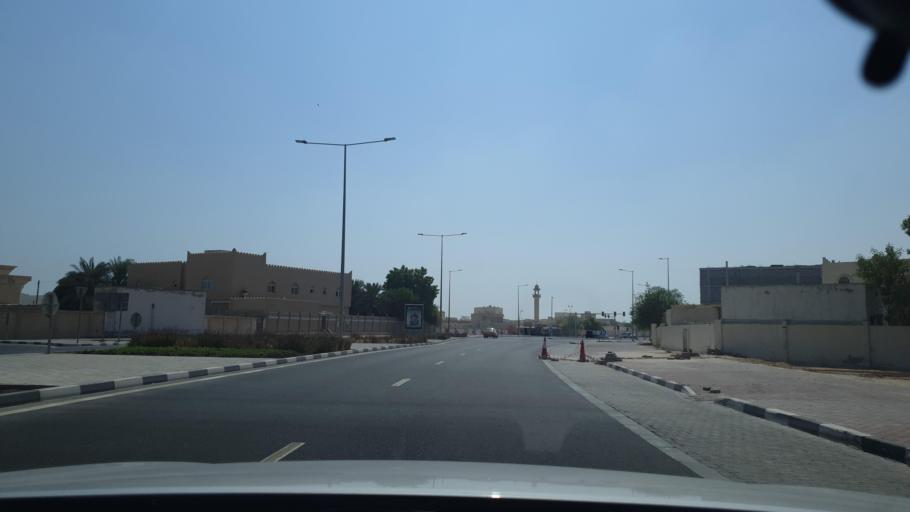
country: QA
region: Al Khawr
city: Al Khawr
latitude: 25.6848
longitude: 51.5157
